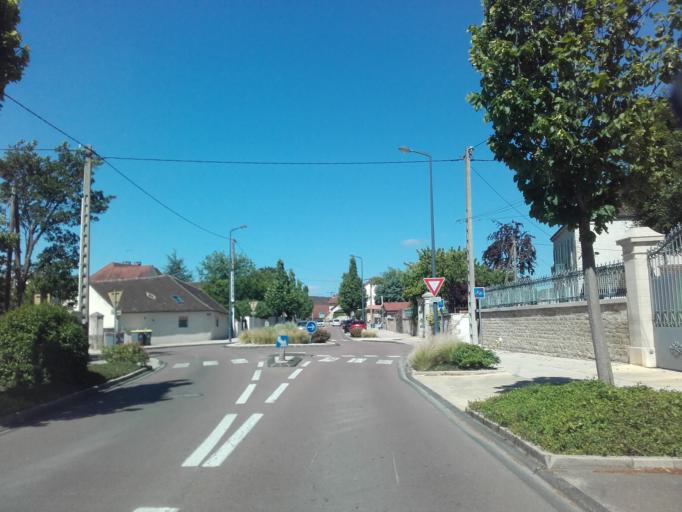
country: FR
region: Bourgogne
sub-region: Departement de la Cote-d'Or
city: Beaune
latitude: 47.0199
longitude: 4.8518
